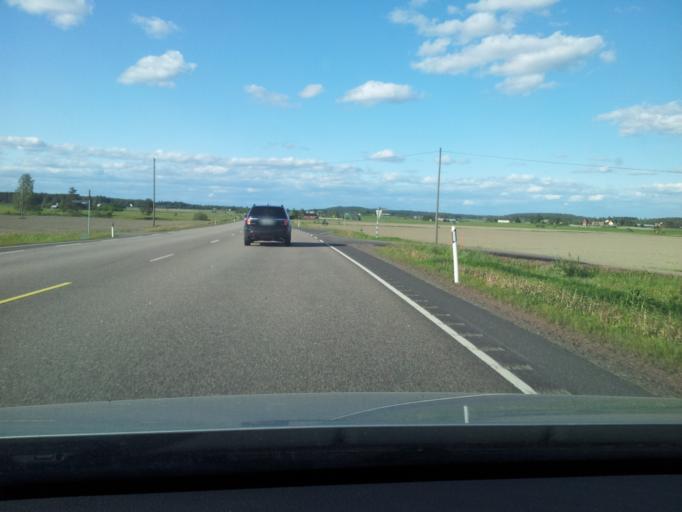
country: FI
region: Kymenlaakso
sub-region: Kouvola
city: Elimaeki
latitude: 60.7383
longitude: 26.4437
